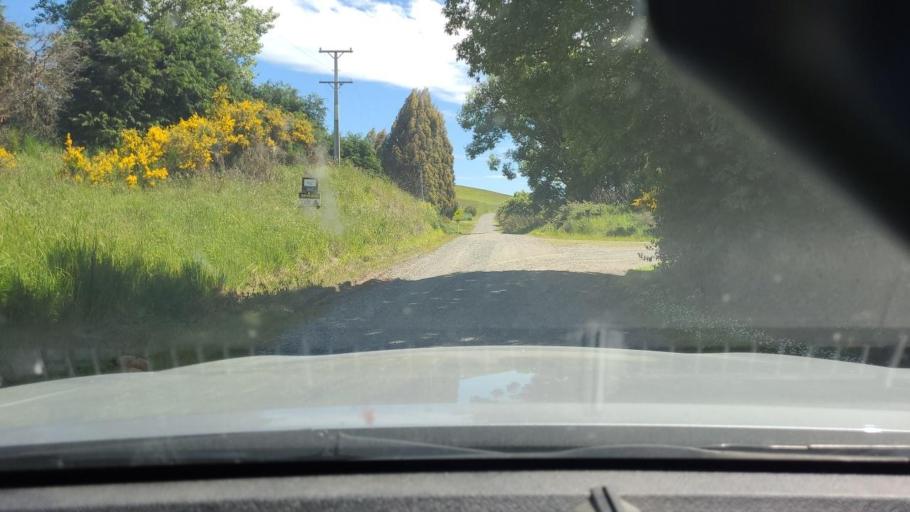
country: NZ
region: Southland
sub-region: Southland District
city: Riverton
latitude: -46.0446
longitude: 167.7845
